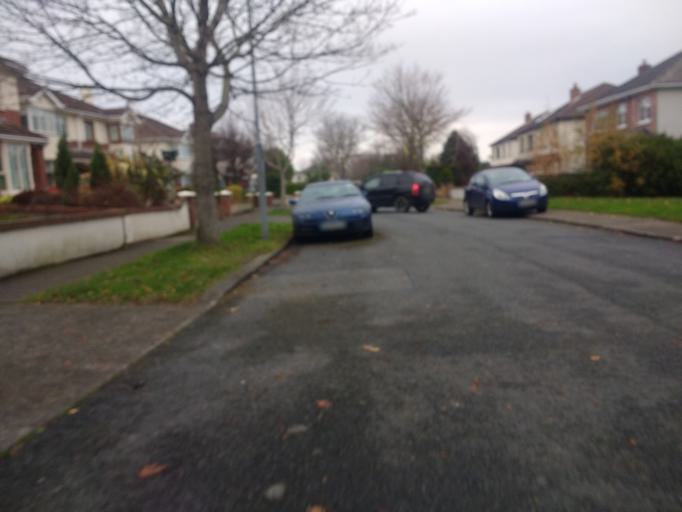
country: IE
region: Leinster
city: Malahide
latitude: 53.4530
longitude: -6.1772
